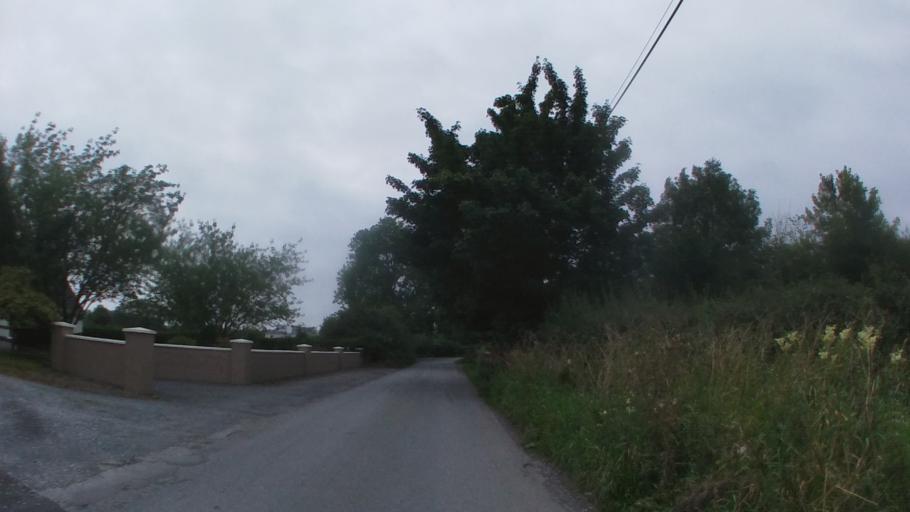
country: IE
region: Leinster
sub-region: Kilkenny
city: Kilkenny
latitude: 52.6982
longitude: -7.2000
